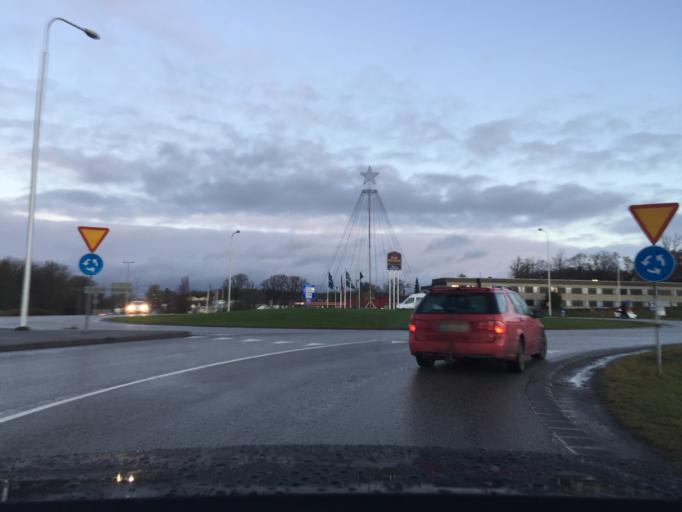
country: SE
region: Blekinge
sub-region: Karlshamns Kommun
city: Karlshamn
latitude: 56.1888
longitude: 14.8467
